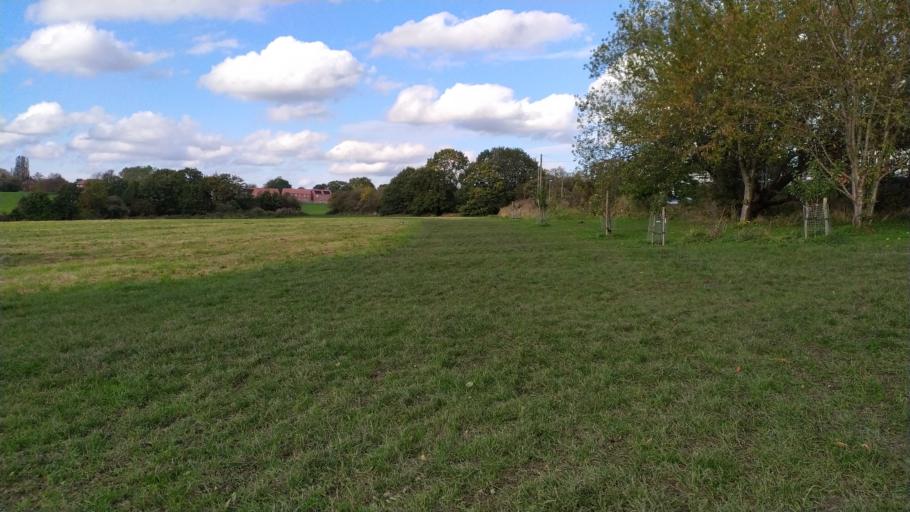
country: GB
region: England
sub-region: City and Borough of Leeds
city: Horsforth
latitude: 53.8298
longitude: -1.5977
